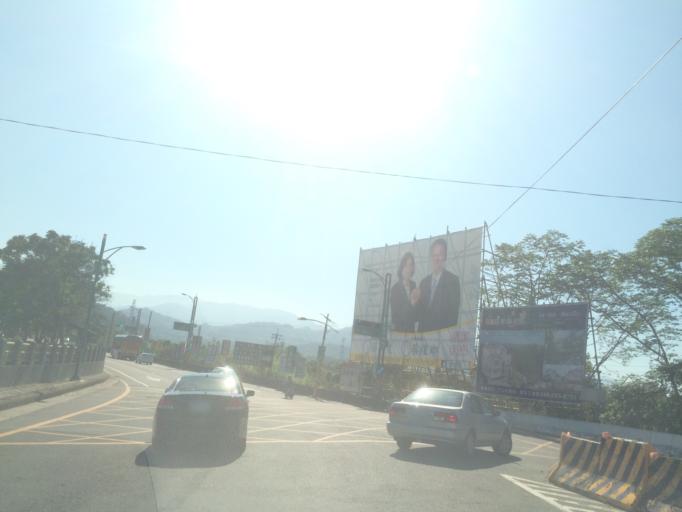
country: TW
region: Taiwan
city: Lugu
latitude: 23.7846
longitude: 120.7049
